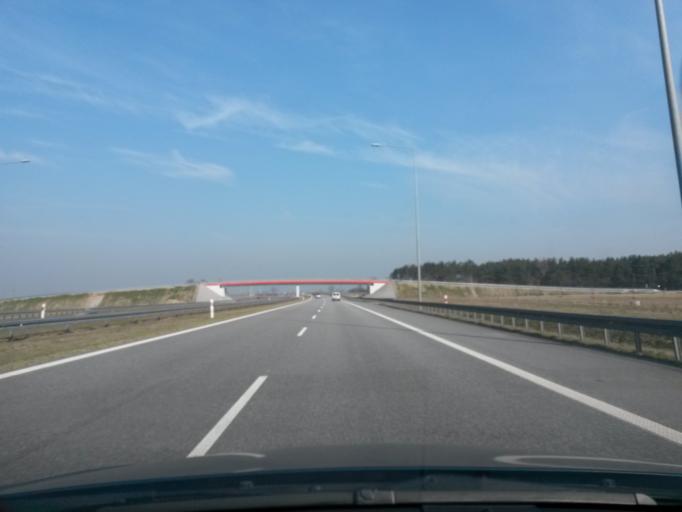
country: PL
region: Lodz Voivodeship
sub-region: Powiat kutnowski
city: Krzyzanow
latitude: 52.1899
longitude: 19.4879
